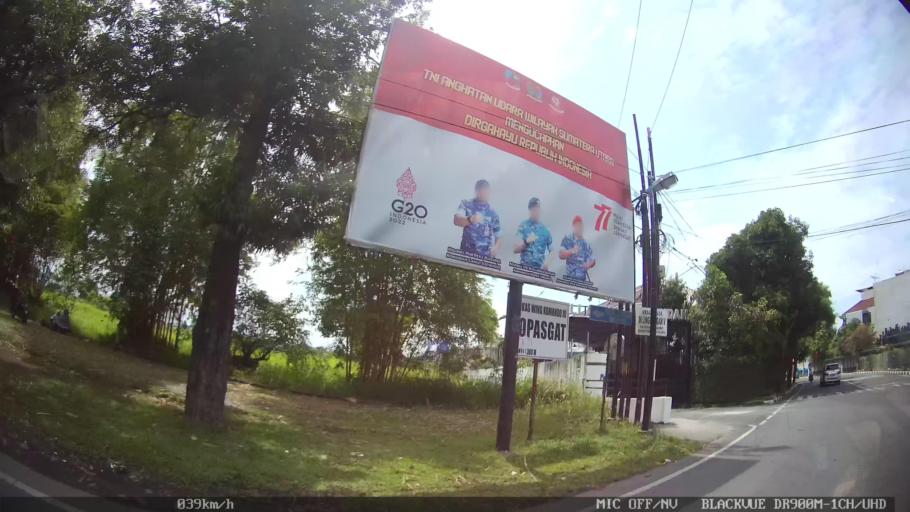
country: ID
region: North Sumatra
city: Medan
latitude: 3.5694
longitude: 98.6733
